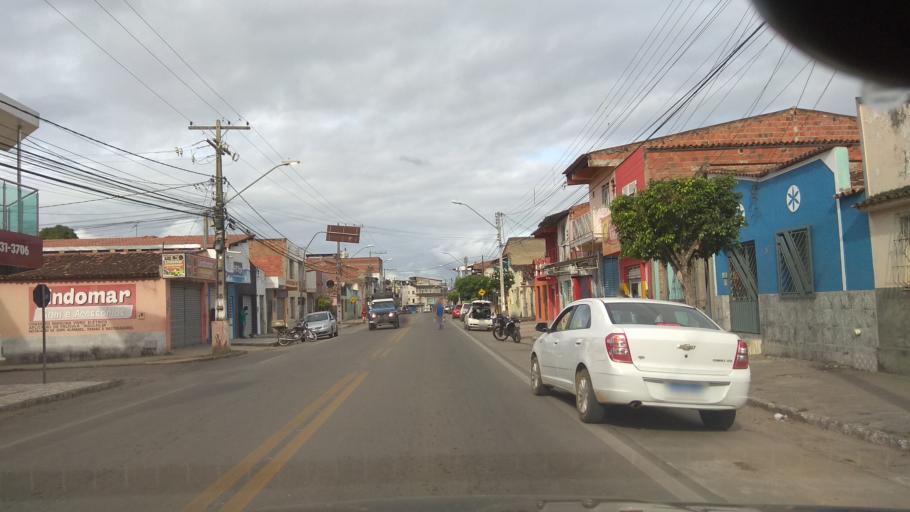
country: BR
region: Bahia
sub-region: Ipiau
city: Ipiau
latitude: -14.1355
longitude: -39.7434
